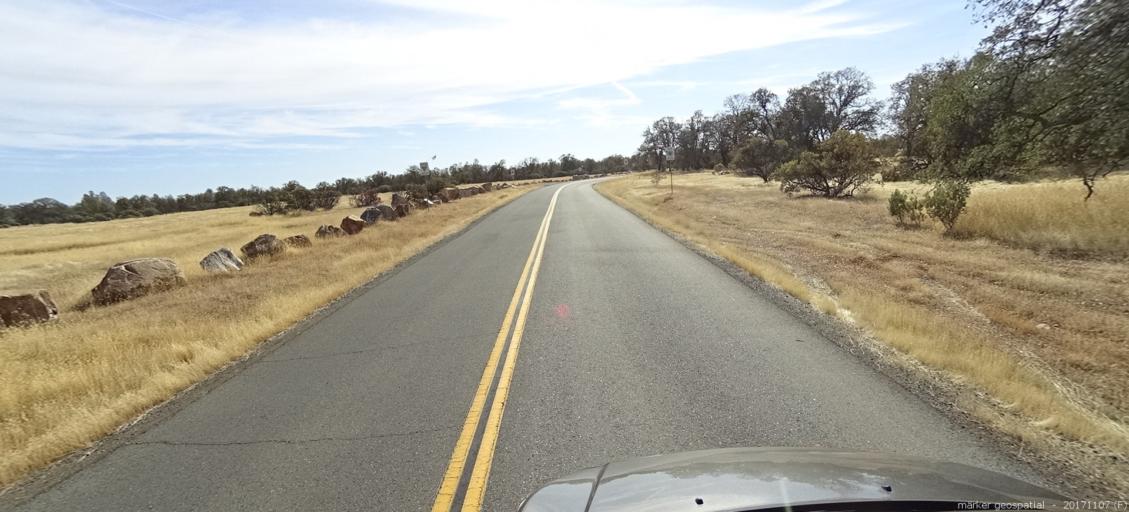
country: US
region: California
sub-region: Shasta County
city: Shasta
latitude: 40.4870
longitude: -122.5477
